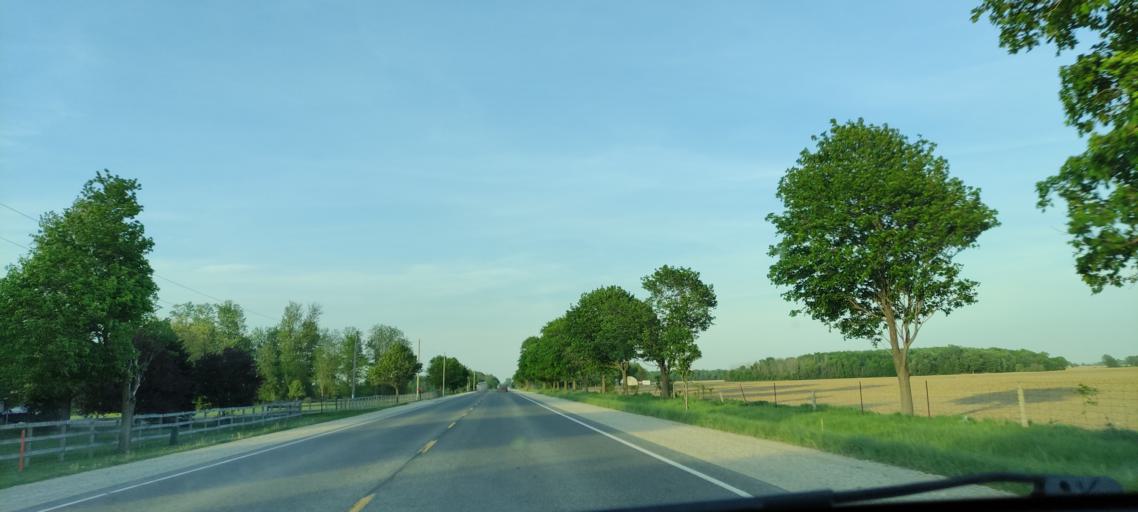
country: CA
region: Ontario
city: London
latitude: 43.1907
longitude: -81.2676
